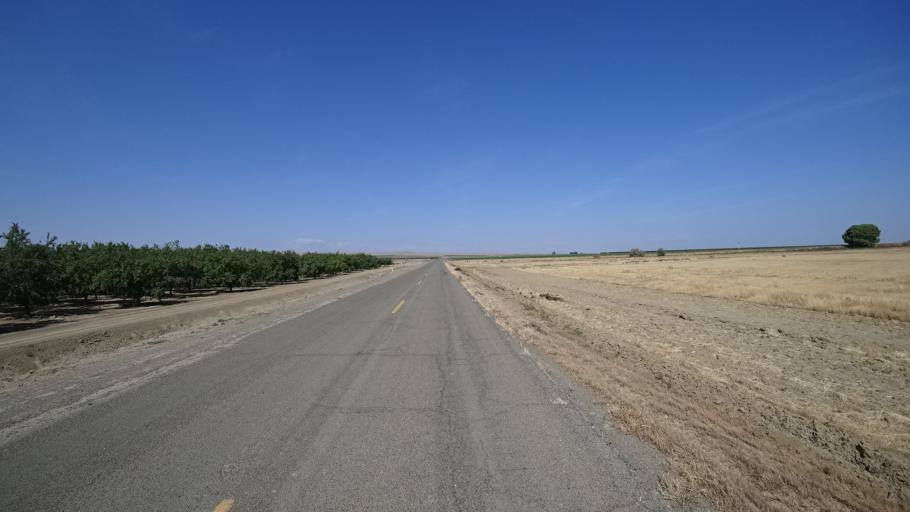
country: US
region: California
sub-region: Kings County
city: Kettleman City
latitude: 36.0364
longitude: -119.9653
